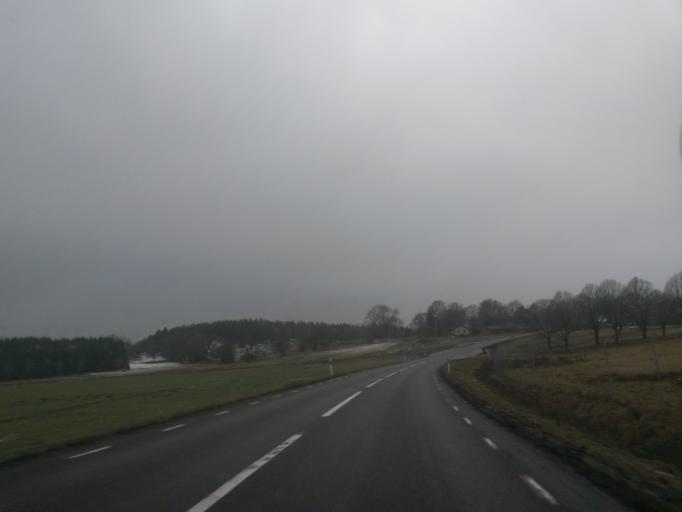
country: SE
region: Vaestra Goetaland
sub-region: Alingsas Kommun
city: Sollebrunn
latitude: 58.1373
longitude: 12.4297
